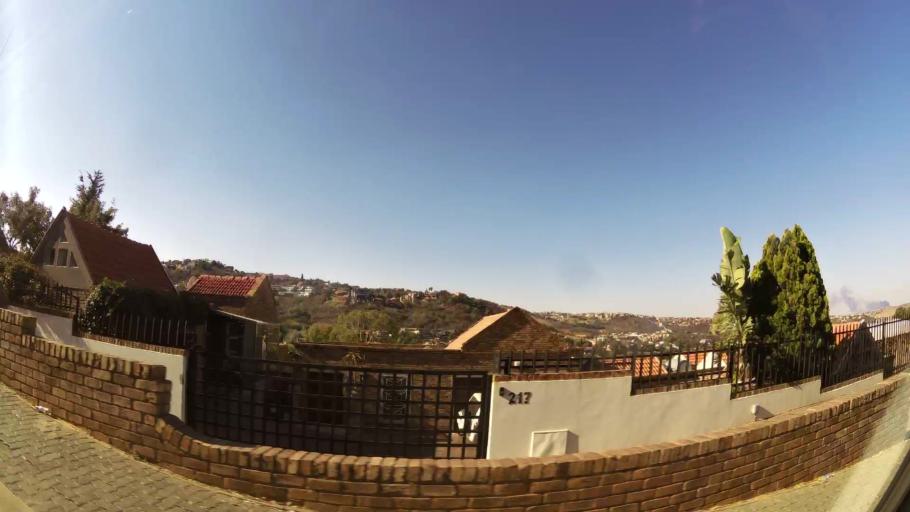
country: ZA
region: Gauteng
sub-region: City of Johannesburg Metropolitan Municipality
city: Johannesburg
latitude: -26.2805
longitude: 28.0545
